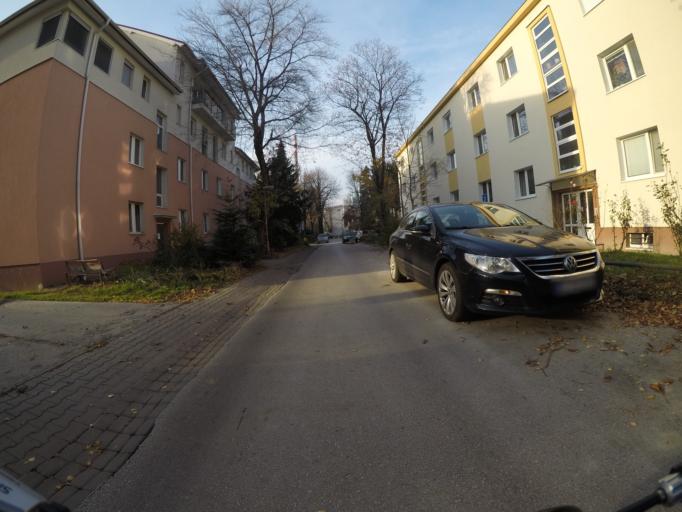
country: SK
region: Bratislavsky
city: Bratislava
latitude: 48.1747
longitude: 17.1576
